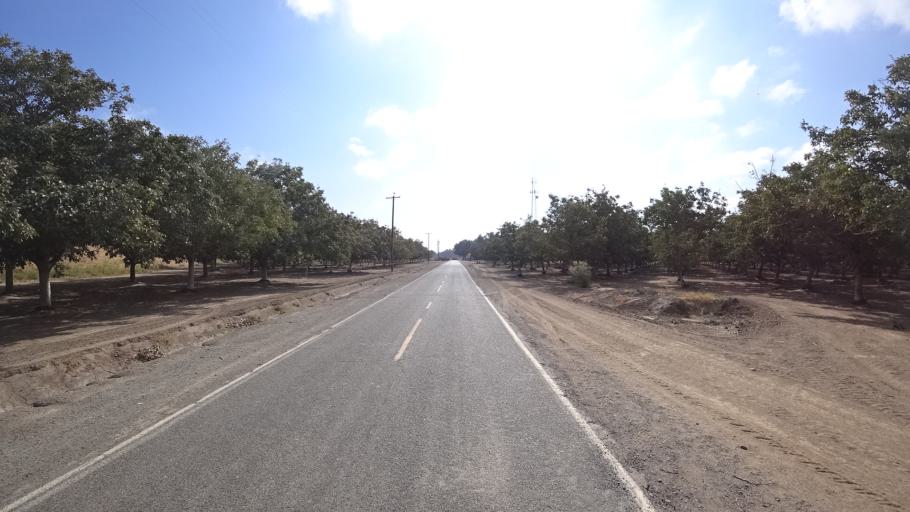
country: US
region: California
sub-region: Yolo County
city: Woodland
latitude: 38.7846
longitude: -121.6947
